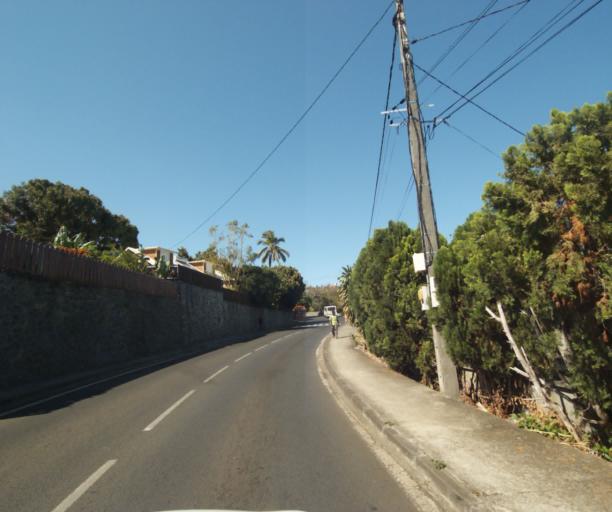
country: RE
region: Reunion
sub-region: Reunion
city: Saint-Paul
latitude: -20.9922
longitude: 55.3304
